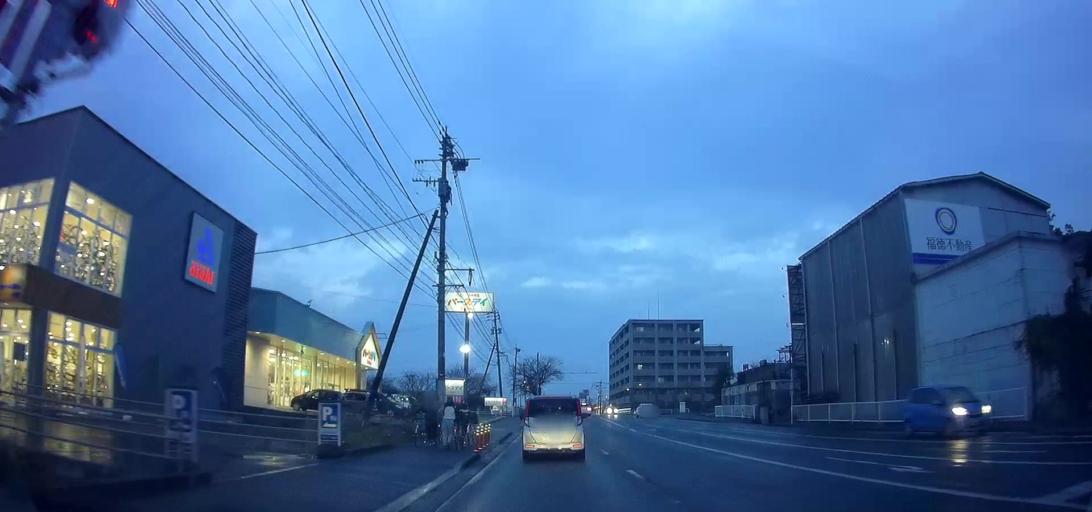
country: JP
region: Nagasaki
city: Omura
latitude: 32.9088
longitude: 129.9546
